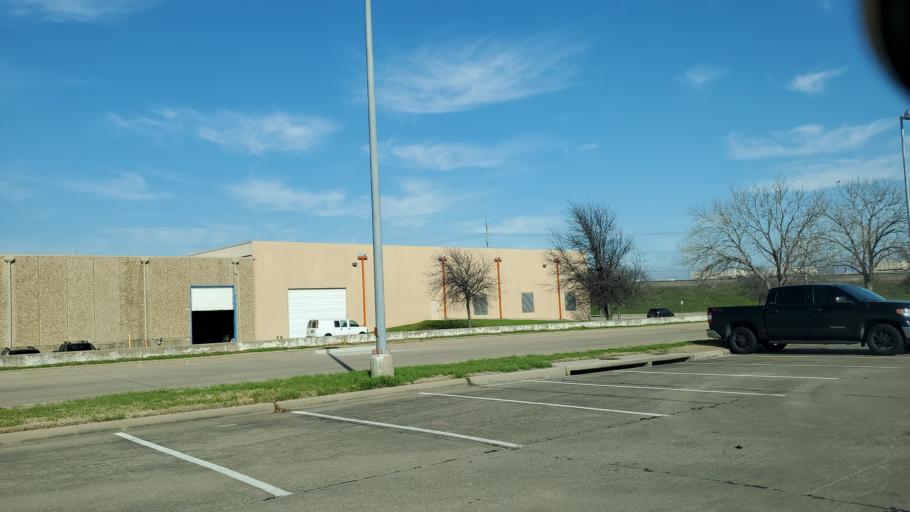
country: US
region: Texas
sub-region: Dallas County
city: Richardson
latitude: 32.9633
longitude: -96.7204
